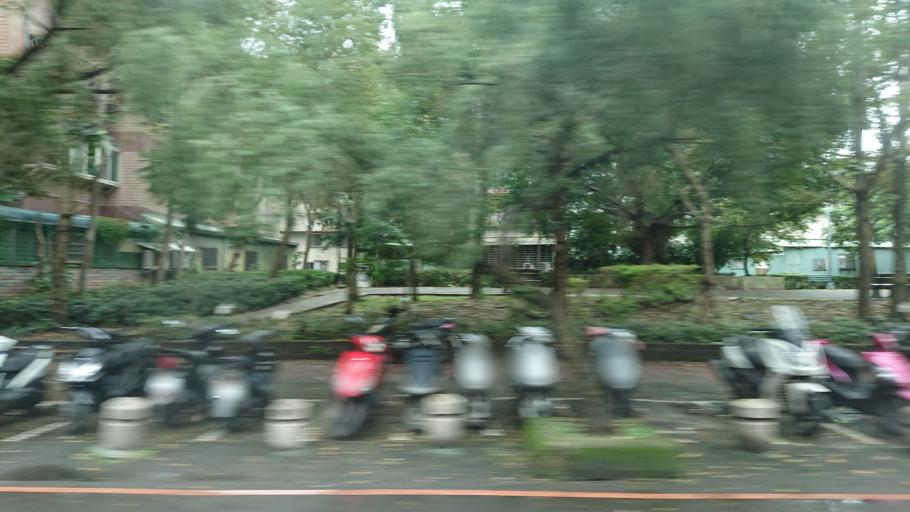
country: TW
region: Taipei
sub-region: Taipei
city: Banqiao
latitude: 24.9850
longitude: 121.4636
